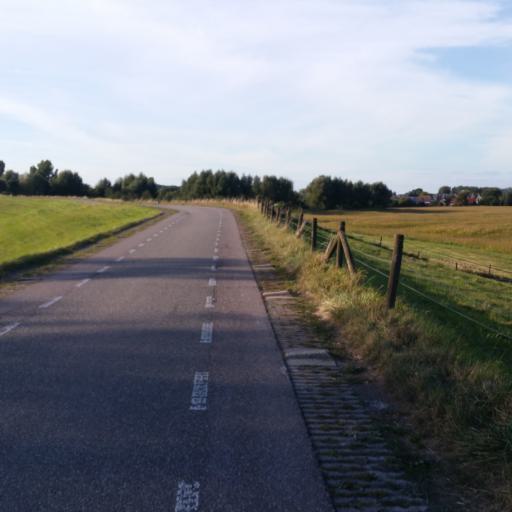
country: NL
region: Utrecht
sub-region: Gemeente IJsselstein
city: IJsselstein
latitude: 51.9776
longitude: 5.0200
